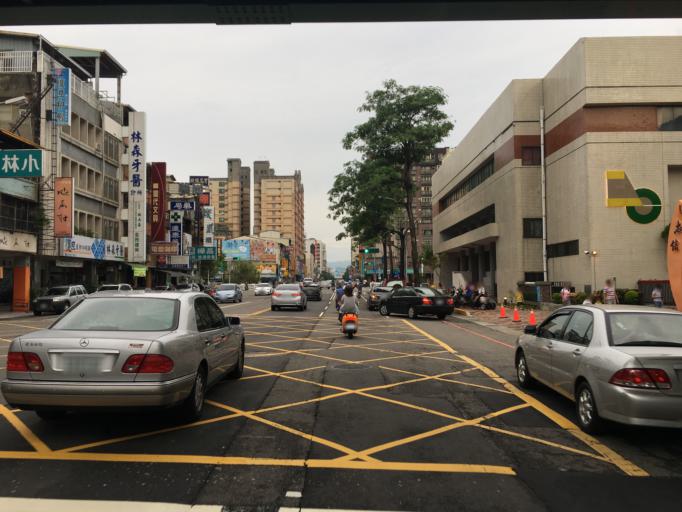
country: TW
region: Taiwan
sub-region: Taichung City
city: Taichung
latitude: 24.1394
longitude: 120.6686
